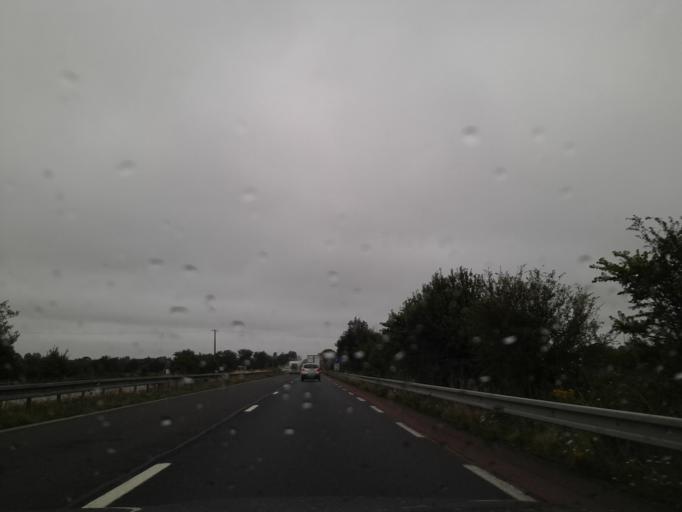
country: FR
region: Lower Normandy
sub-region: Departement de la Manche
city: Sainte-Mere-Eglise
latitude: 49.4473
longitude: -1.3474
